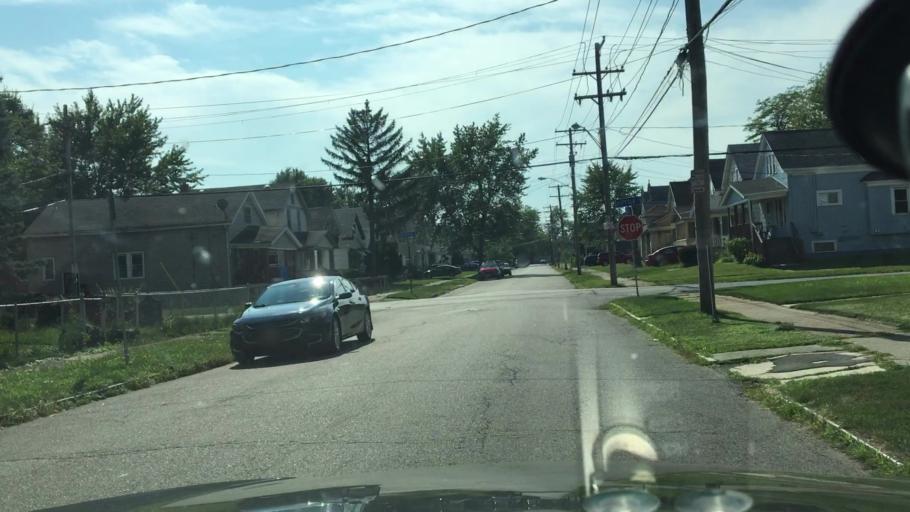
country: US
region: New York
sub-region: Erie County
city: Eggertsville
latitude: 42.9366
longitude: -78.8100
